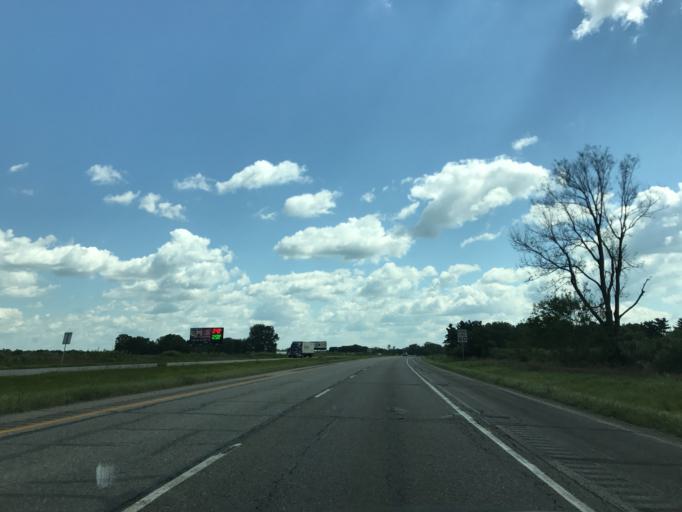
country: US
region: Indiana
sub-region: Marshall County
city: Plymouth
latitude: 41.3623
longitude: -86.3025
